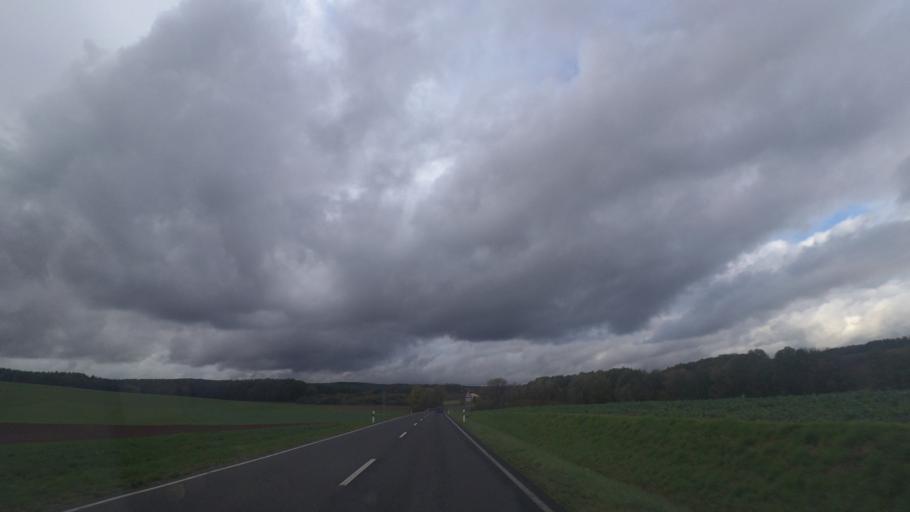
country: DE
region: Bavaria
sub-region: Regierungsbezirk Unterfranken
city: Hohenroth
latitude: 50.3281
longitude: 10.1559
